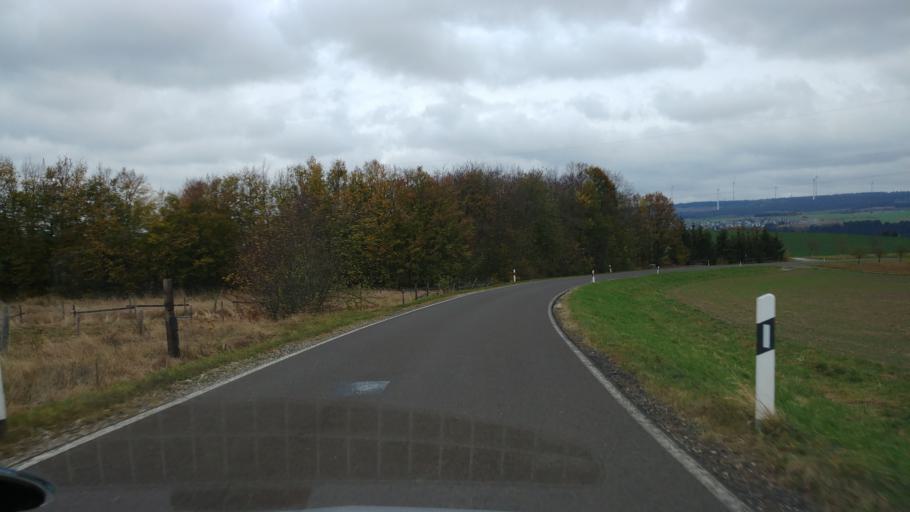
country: DE
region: Rheinland-Pfalz
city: Rorodt
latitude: 49.7859
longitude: 7.0525
